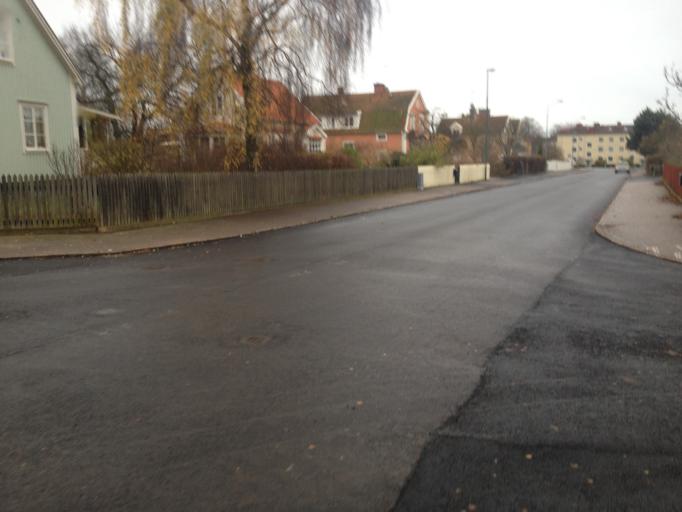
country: SE
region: Kalmar
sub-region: Kalmar Kommun
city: Kalmar
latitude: 56.6758
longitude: 16.3523
